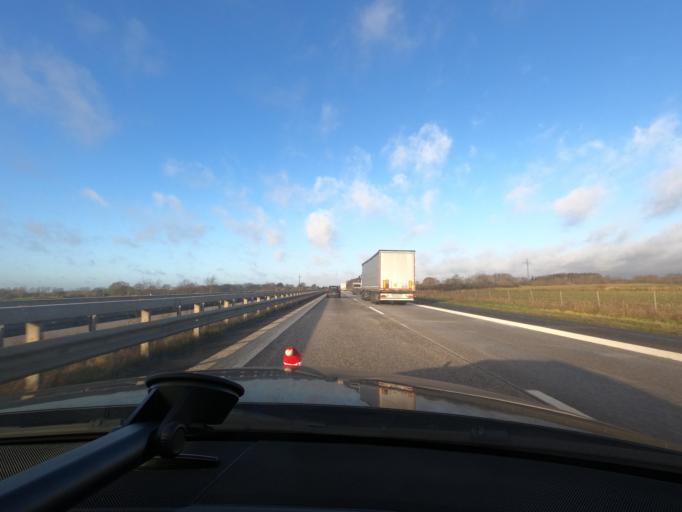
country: DE
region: Schleswig-Holstein
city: Lottorf
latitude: 54.4374
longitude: 9.5924
